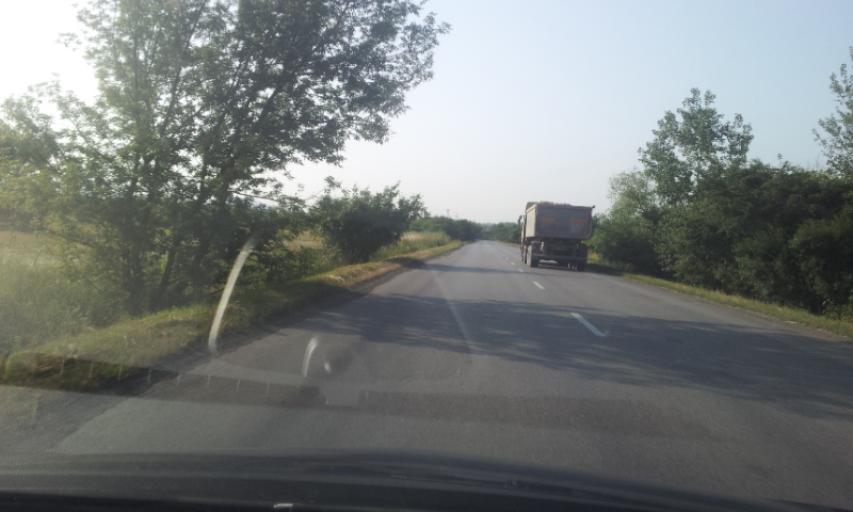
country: SK
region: Kosicky
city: Kosice
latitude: 48.6264
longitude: 21.2222
